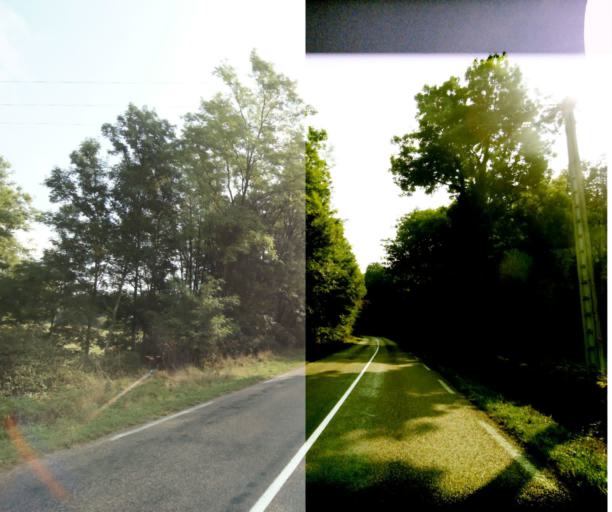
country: FR
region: Bourgogne
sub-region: Departement de Saone-et-Loire
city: Charolles
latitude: 46.4236
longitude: 4.2695
